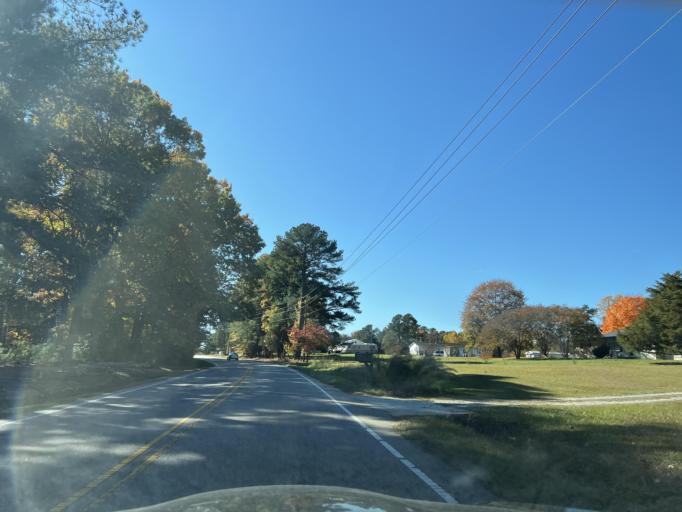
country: US
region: North Carolina
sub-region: Wake County
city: Garner
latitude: 35.6806
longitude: -78.6997
